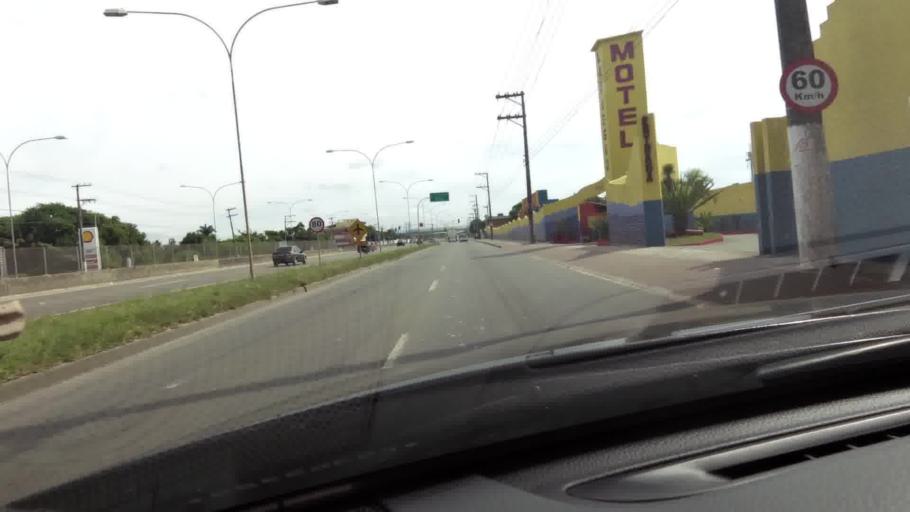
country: BR
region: Espirito Santo
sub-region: Vila Velha
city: Vila Velha
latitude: -20.4238
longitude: -40.3293
